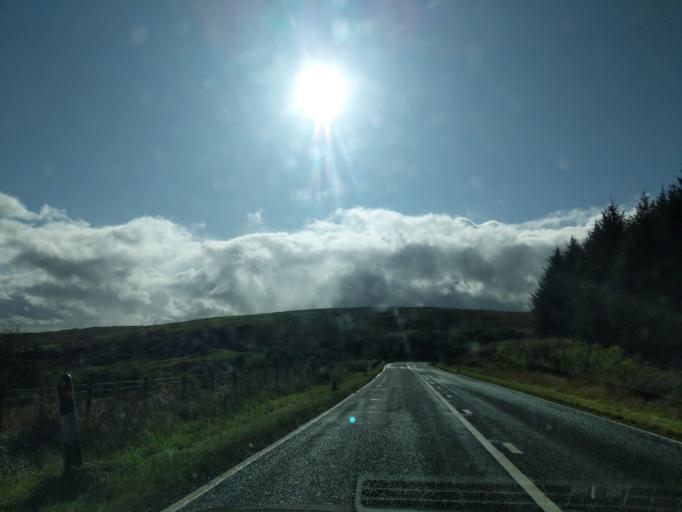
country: GB
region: Scotland
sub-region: Dumfries and Galloway
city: Moffat
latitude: 55.3652
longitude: -3.4754
